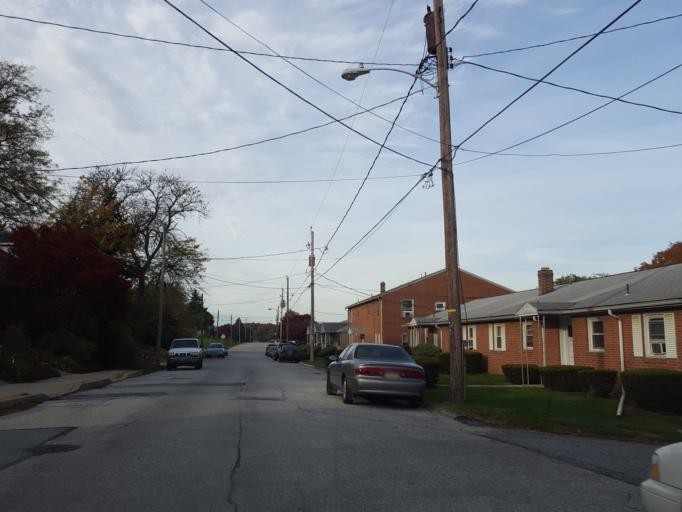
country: US
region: Pennsylvania
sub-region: York County
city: Red Lion
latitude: 39.9045
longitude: -76.6118
